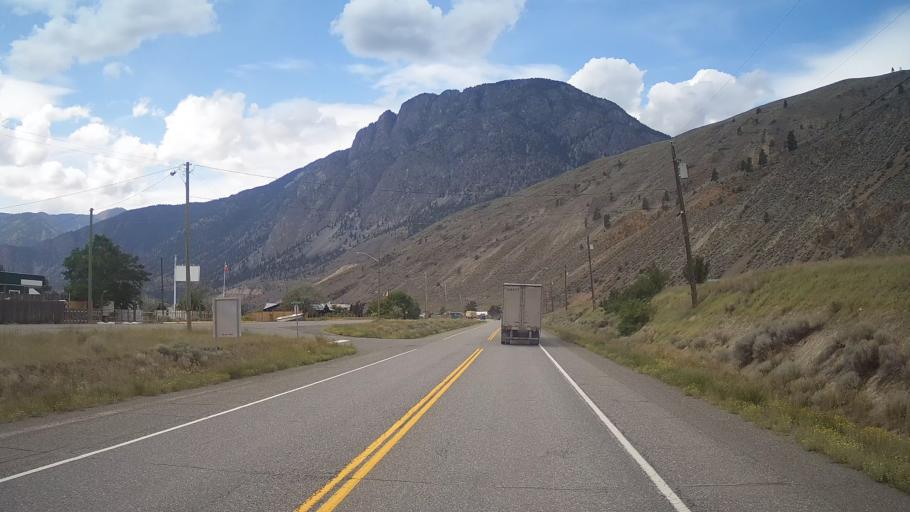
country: CA
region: British Columbia
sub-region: Thompson-Nicola Regional District
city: Ashcroft
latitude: 50.4251
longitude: -121.3366
